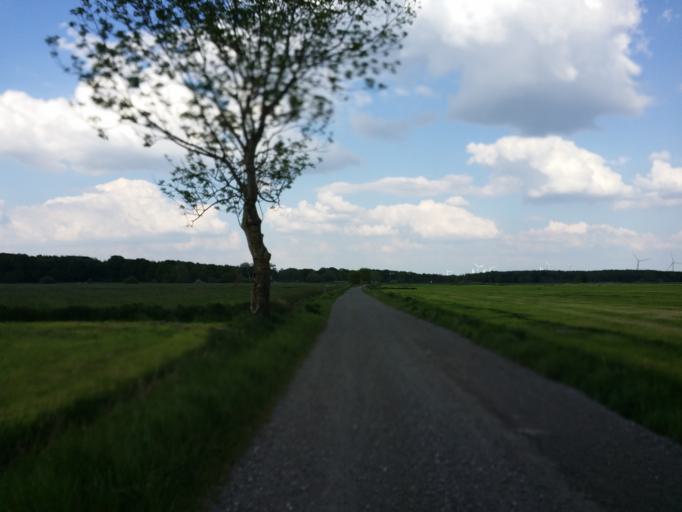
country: DE
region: Lower Saxony
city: Loxstedt
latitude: 53.4465
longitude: 8.6495
